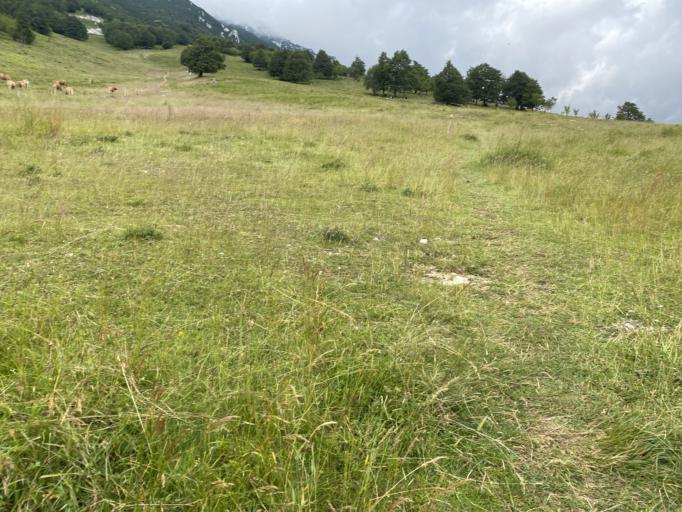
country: IT
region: Veneto
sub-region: Provincia di Verona
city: Ferrara di Monte Baldo
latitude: 45.7099
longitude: 10.8593
